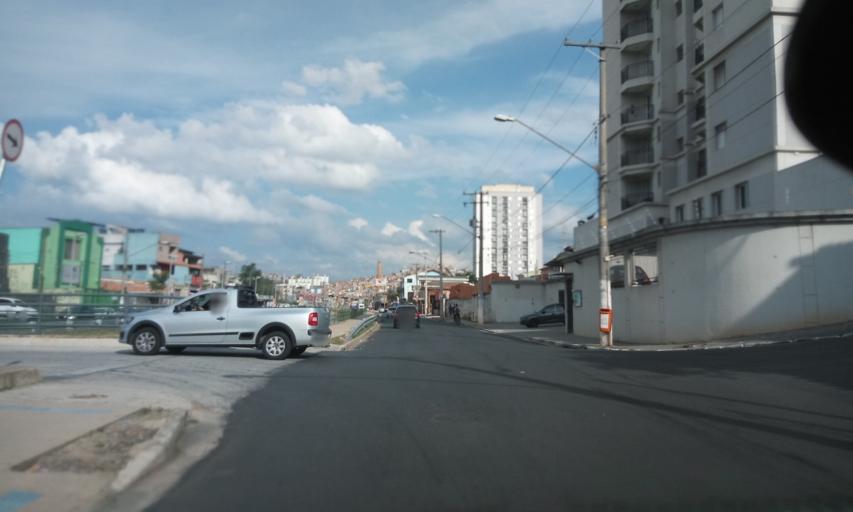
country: BR
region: Sao Paulo
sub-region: Sao Bernardo Do Campo
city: Sao Bernardo do Campo
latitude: -23.7046
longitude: -46.5381
